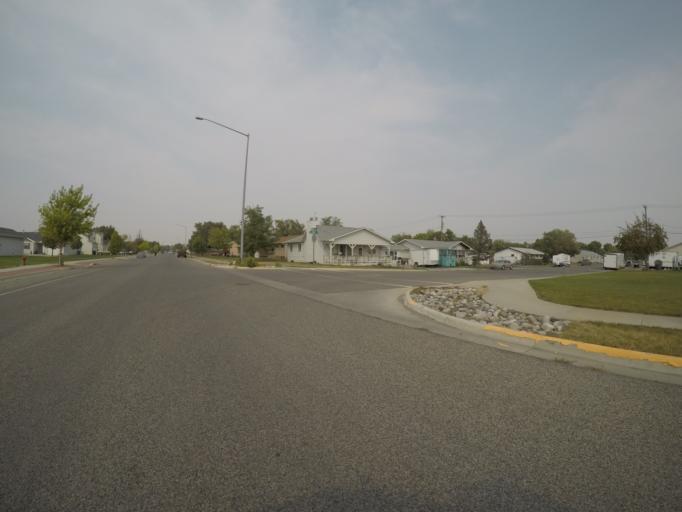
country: US
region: Montana
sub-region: Yellowstone County
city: Laurel
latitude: 45.6692
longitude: -108.7820
